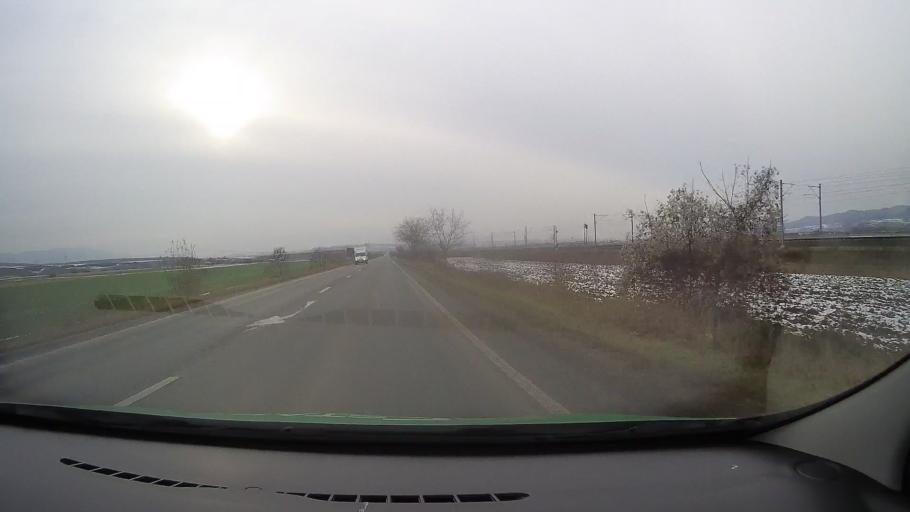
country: RO
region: Hunedoara
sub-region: Comuna Geoagiu
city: Geoagiu
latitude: 45.8806
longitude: 23.2444
